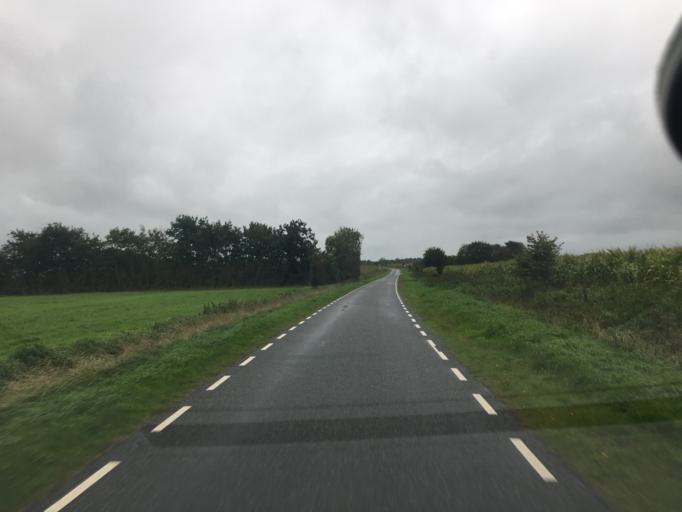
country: DE
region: Schleswig-Holstein
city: Ellhoft
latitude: 54.9378
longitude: 8.9460
